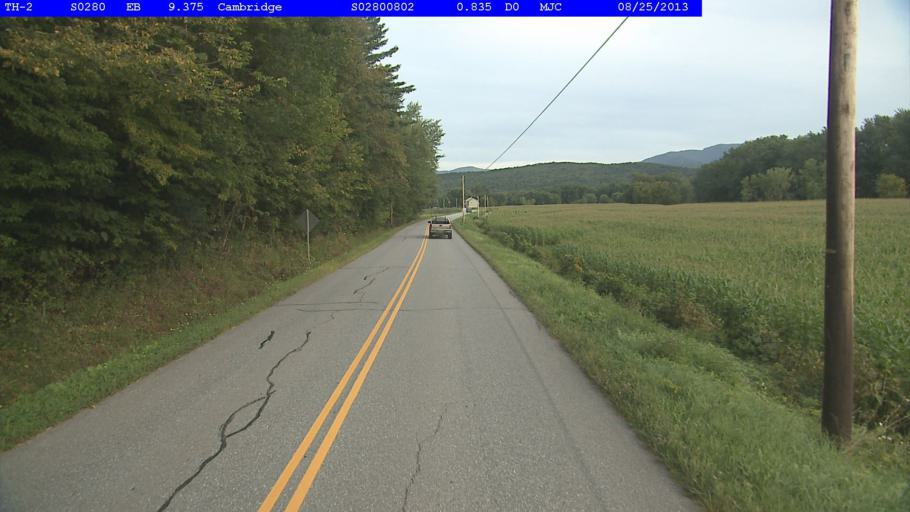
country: US
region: Vermont
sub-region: Chittenden County
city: Jericho
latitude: 44.6518
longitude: -72.8792
